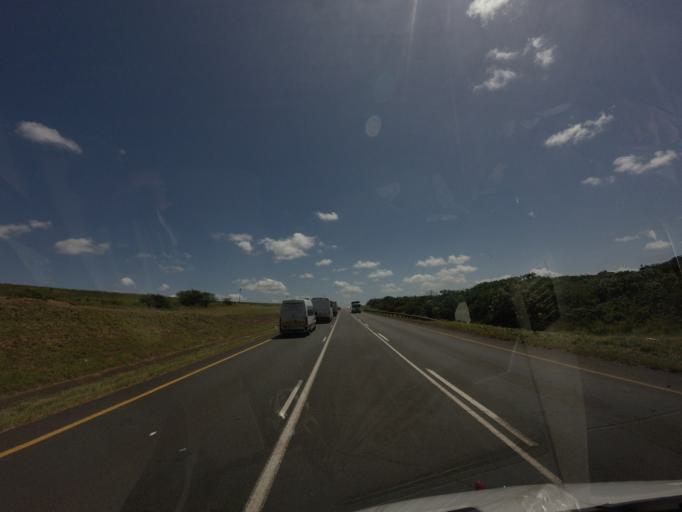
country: ZA
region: KwaZulu-Natal
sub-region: uThungulu District Municipality
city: Empangeni
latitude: -28.7776
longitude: 31.9279
